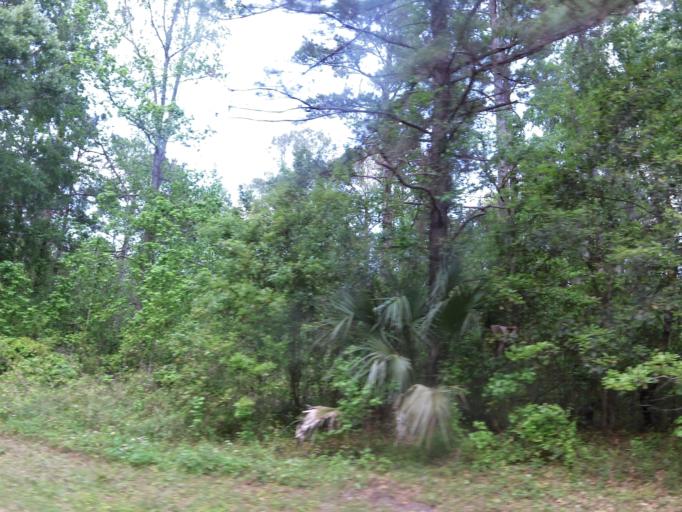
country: US
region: Georgia
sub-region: Camden County
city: Kingsland
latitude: 30.7866
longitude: -81.7056
